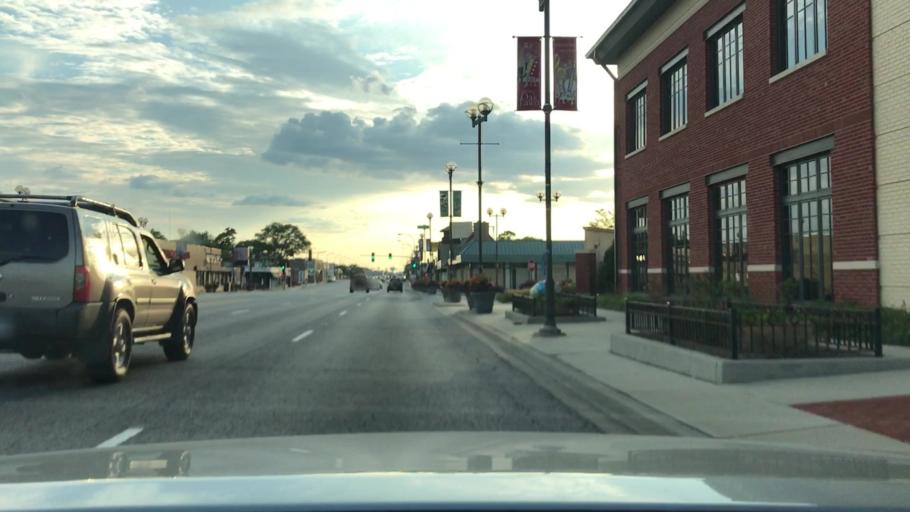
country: US
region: Illinois
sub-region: Cook County
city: Oak Lawn
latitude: 41.7200
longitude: -87.7535
